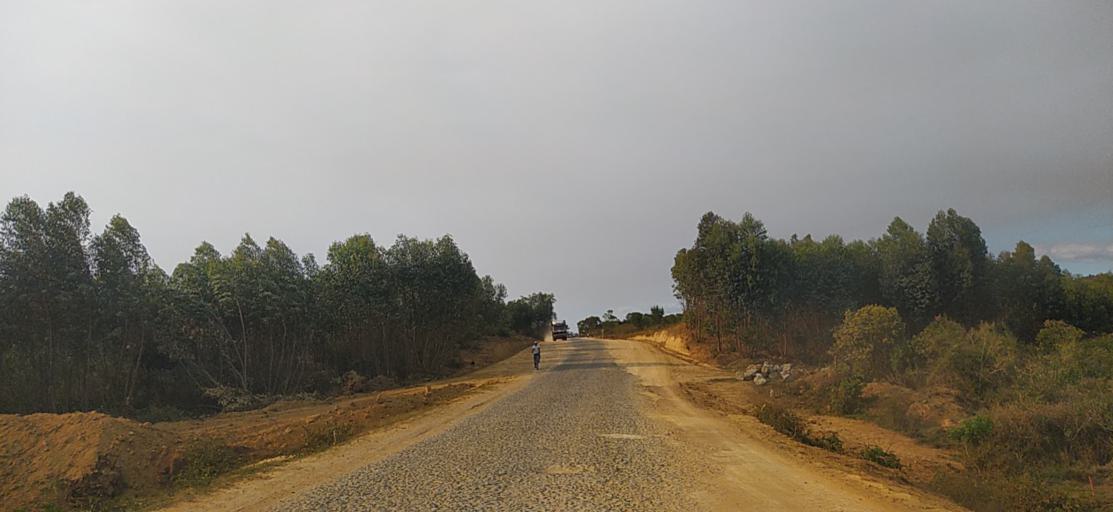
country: MG
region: Alaotra Mangoro
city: Moramanga
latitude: -18.6401
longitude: 48.2757
